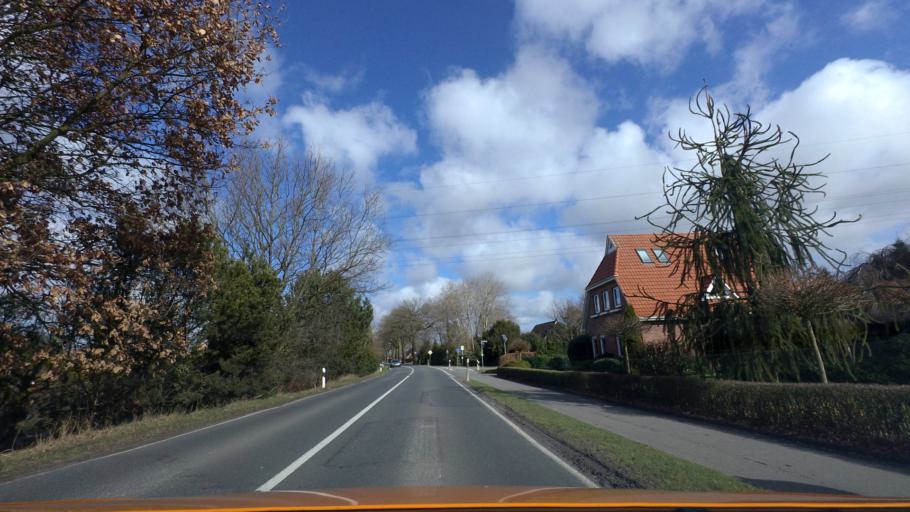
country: DE
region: Lower Saxony
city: Bad Zwischenahn
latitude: 53.1635
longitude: 7.9983
